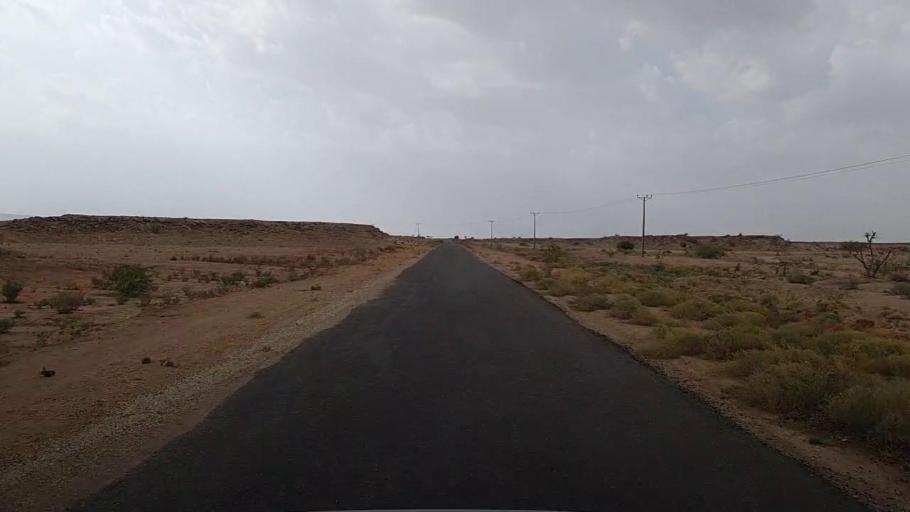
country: PK
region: Sindh
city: Jamshoro
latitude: 25.4280
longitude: 67.6889
